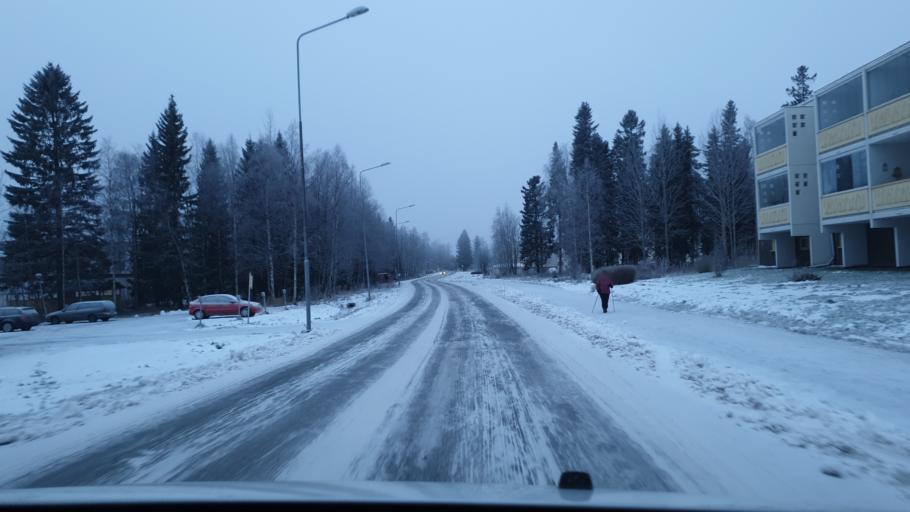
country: FI
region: Lapland
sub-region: Kemi-Tornio
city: Kemi
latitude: 65.7335
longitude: 24.6081
